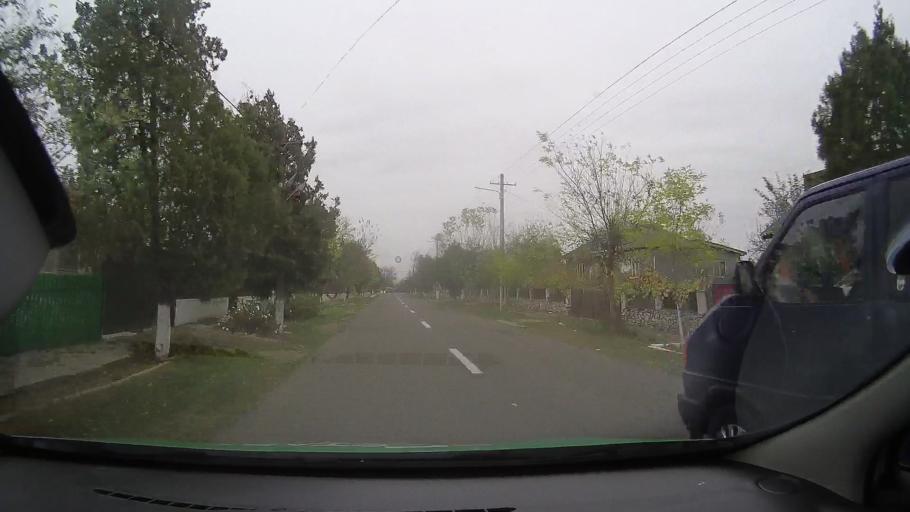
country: RO
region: Constanta
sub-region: Comuna Vulturu
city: Vulturu
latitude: 44.7030
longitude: 28.2342
